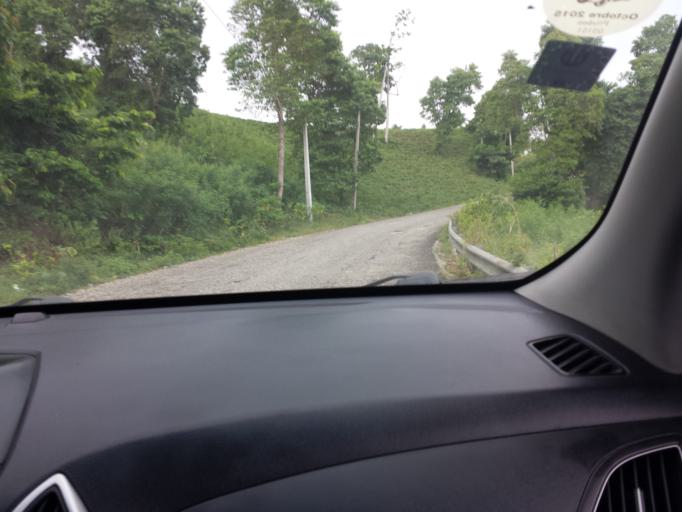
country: HT
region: Ouest
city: Leogane
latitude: 18.3864
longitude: -72.6065
